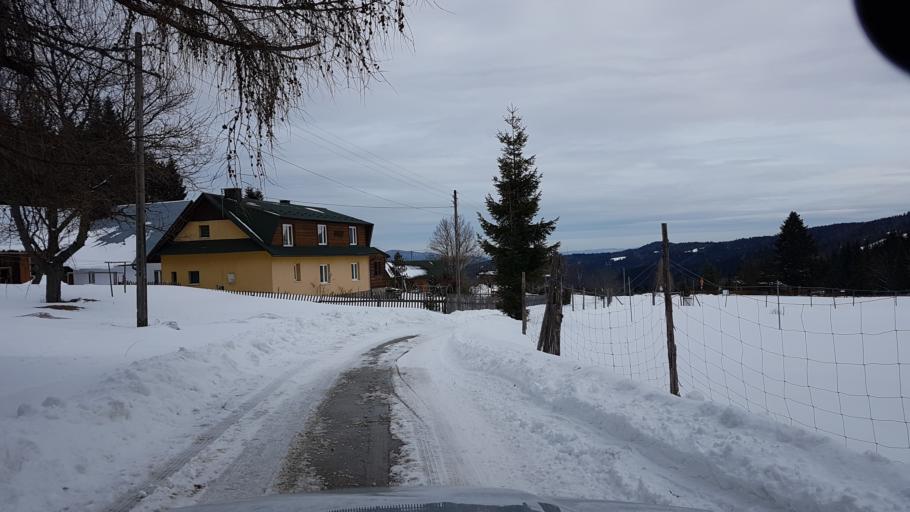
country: PL
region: Lesser Poland Voivodeship
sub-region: Powiat nowosadecki
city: Rytro
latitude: 49.4195
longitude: 20.6193
